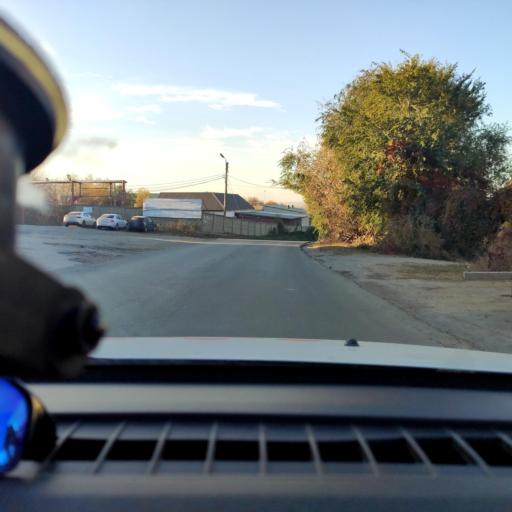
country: RU
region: Samara
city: Samara
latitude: 53.1787
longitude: 50.1562
